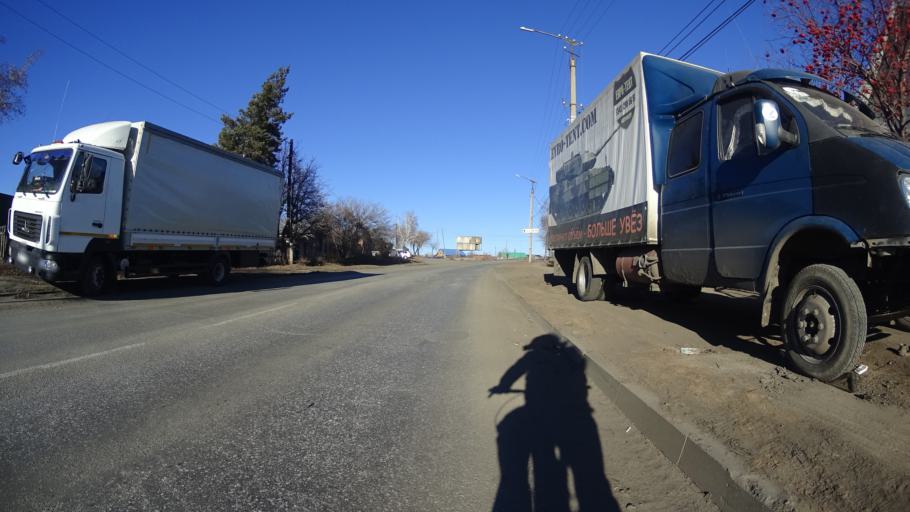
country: RU
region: Chelyabinsk
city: Troitsk
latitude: 54.1026
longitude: 61.5622
